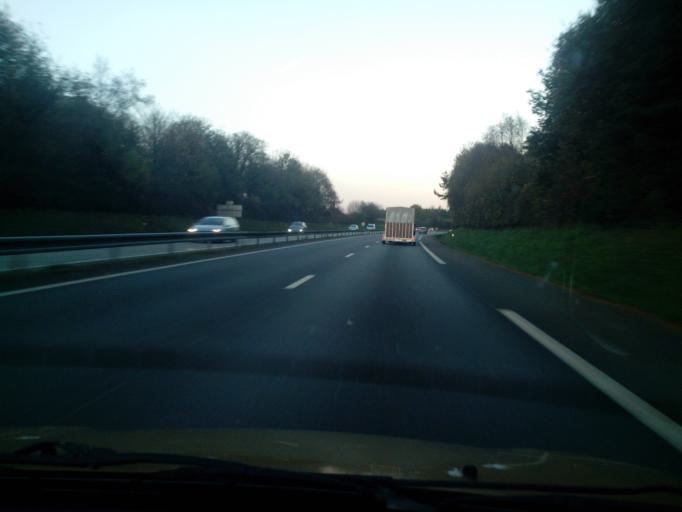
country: FR
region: Brittany
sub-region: Departement du Morbihan
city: Baud
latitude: 47.8928
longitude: -3.0232
